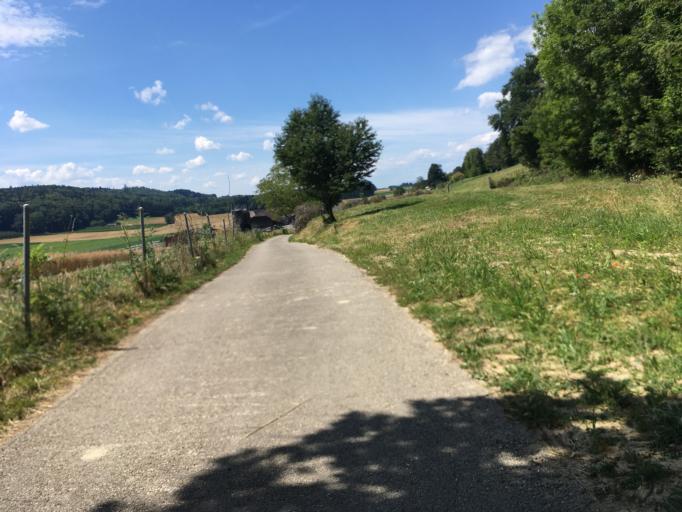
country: CH
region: Neuchatel
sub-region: Neuchatel District
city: Saint-Blaise
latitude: 46.9448
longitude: 7.0027
